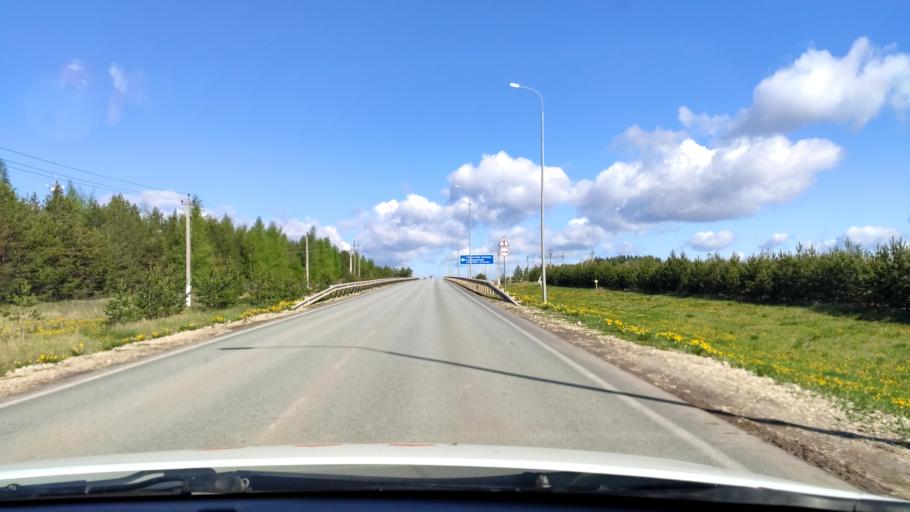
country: RU
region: Tatarstan
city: Sviyazhsk
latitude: 55.7285
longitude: 48.7455
